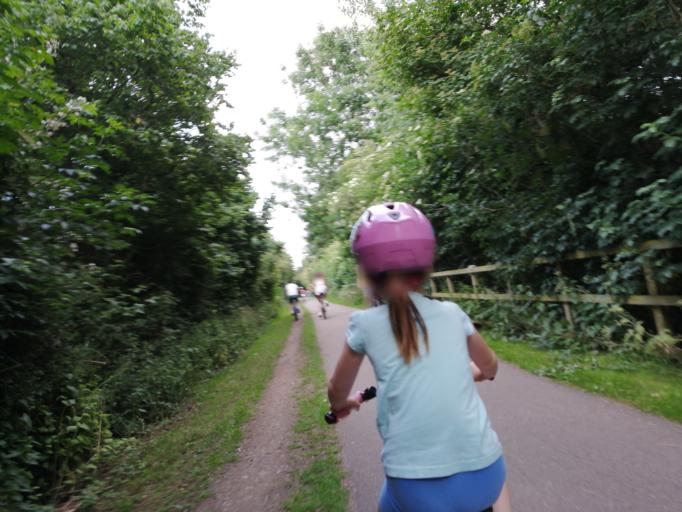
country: GB
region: England
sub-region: Peterborough
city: Peterborough
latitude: 52.5582
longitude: -0.2906
